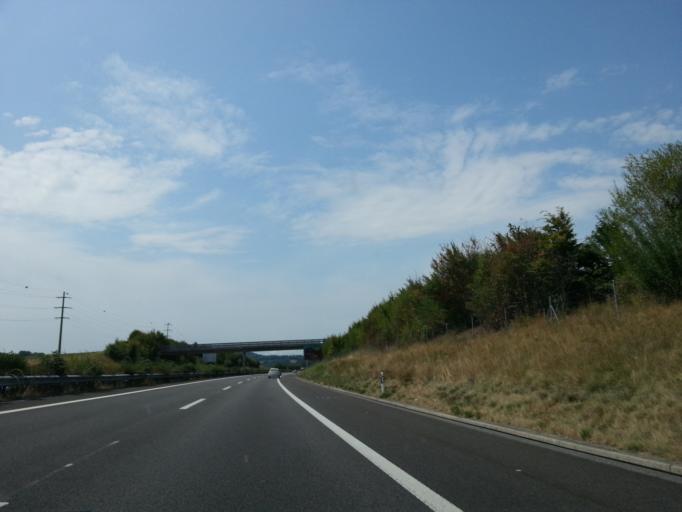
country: CH
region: Fribourg
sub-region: Broye District
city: Cugy
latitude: 46.8255
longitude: 6.8984
